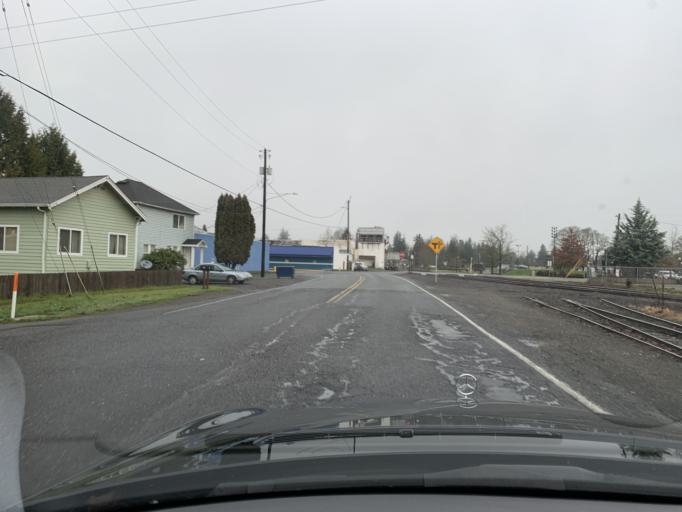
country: US
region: Washington
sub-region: Clark County
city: Battle Ground
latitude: 45.7803
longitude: -122.5284
